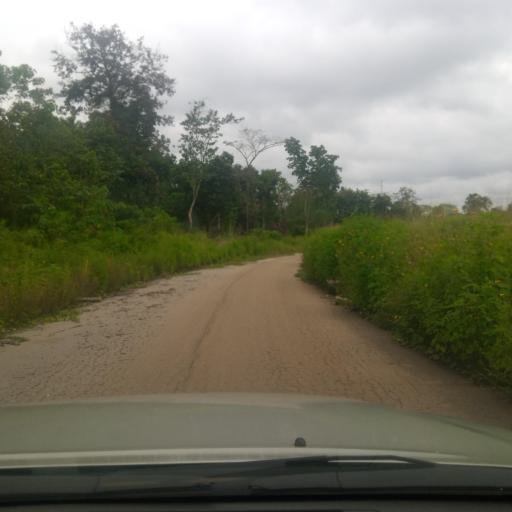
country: NG
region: Ebonyi
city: Effium
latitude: 6.6266
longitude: 8.0501
